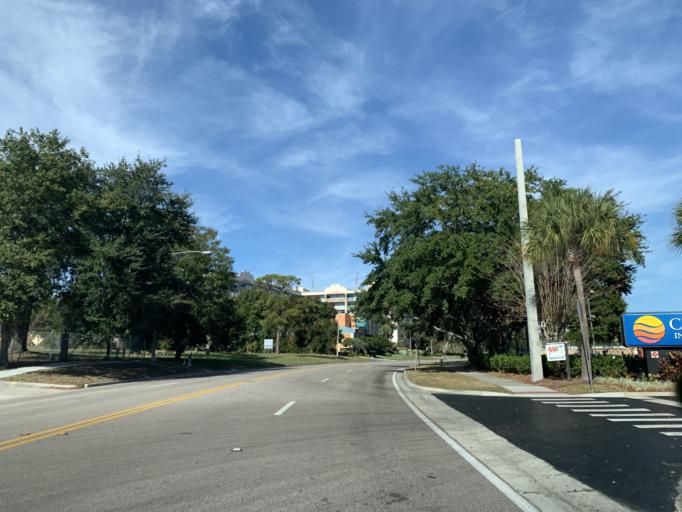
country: US
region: Florida
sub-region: Orange County
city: Tangelo Park
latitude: 28.4528
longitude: -81.4684
